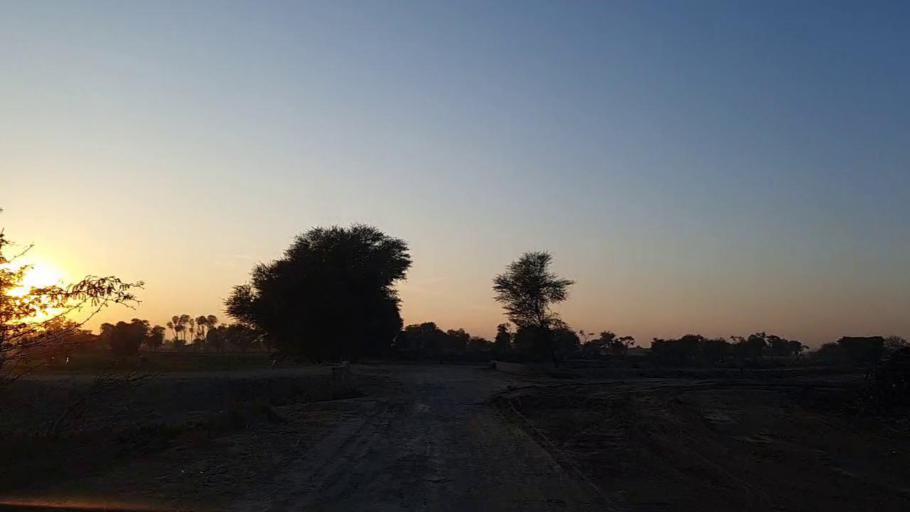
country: PK
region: Sindh
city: Bandhi
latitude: 26.6205
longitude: 68.3499
